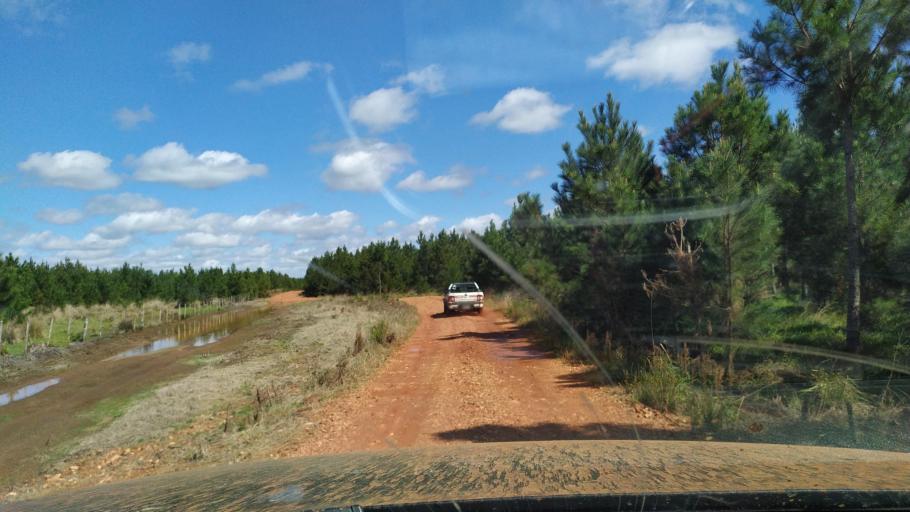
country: AR
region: Corrientes
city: Santo Tome
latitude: -28.4646
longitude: -55.9762
